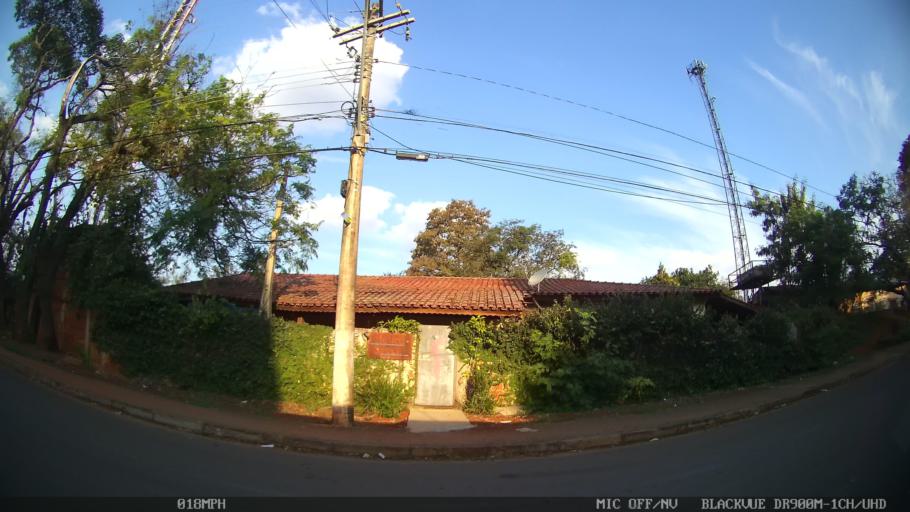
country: BR
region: Sao Paulo
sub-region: Hortolandia
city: Hortolandia
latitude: -22.8638
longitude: -47.1494
